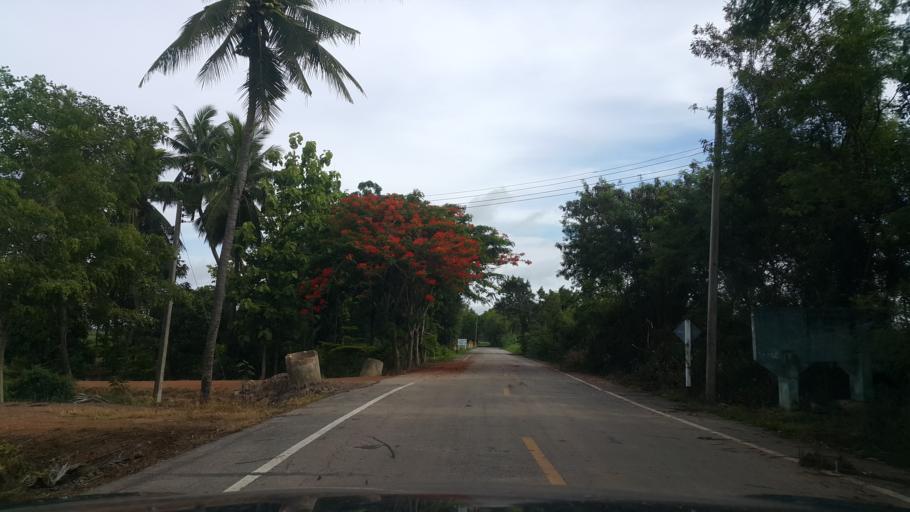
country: TH
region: Sukhothai
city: Si Nakhon
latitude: 17.2663
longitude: 99.9336
